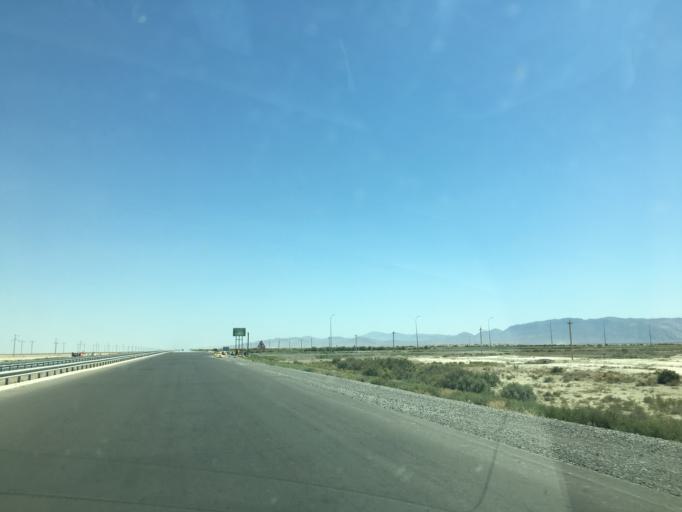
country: TM
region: Balkan
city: Serdar
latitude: 39.0606
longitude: 56.1032
